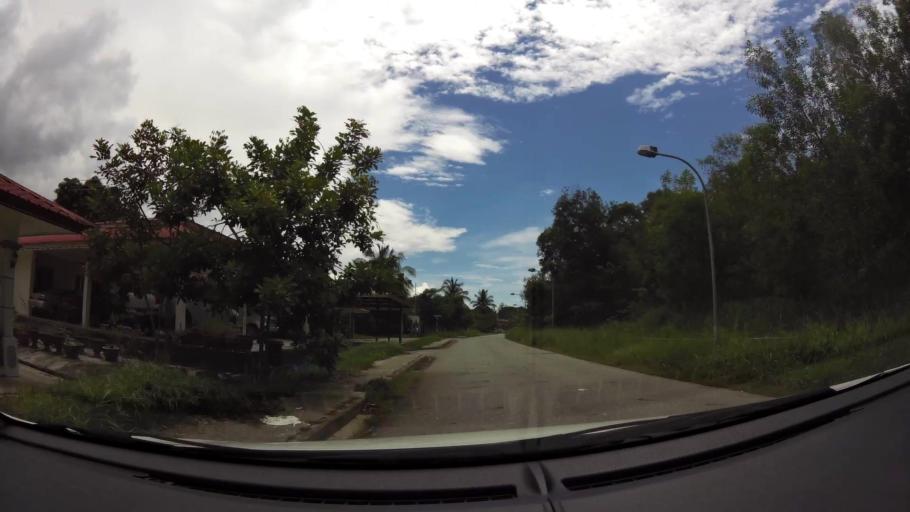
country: BN
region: Brunei and Muara
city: Bandar Seri Begawan
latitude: 4.9836
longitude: 114.9335
